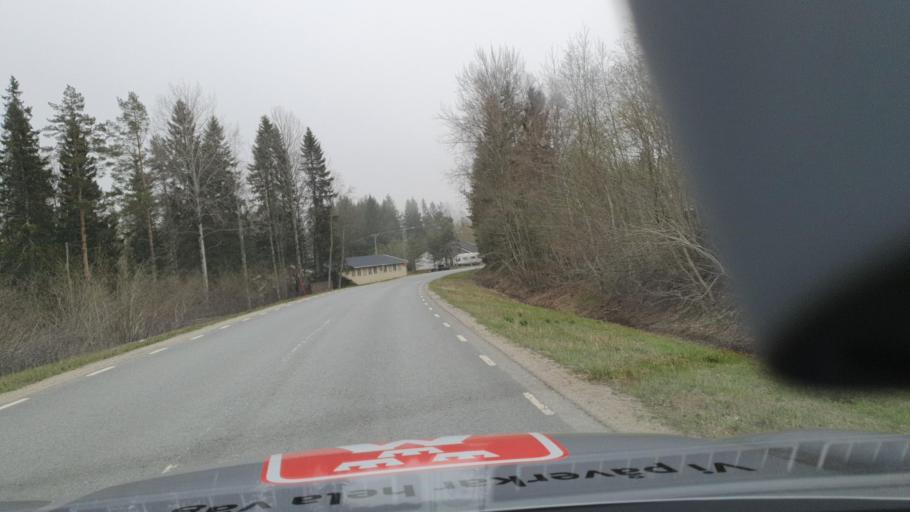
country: SE
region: Vaesternorrland
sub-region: OErnskoeldsviks Kommun
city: Husum
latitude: 63.4853
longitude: 18.9753
